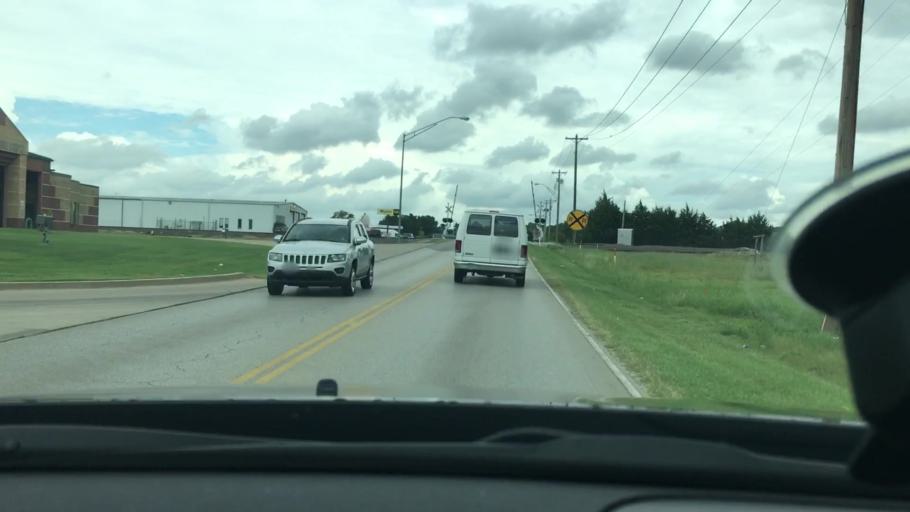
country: US
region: Oklahoma
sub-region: Carter County
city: Ardmore
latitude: 34.1771
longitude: -97.1605
